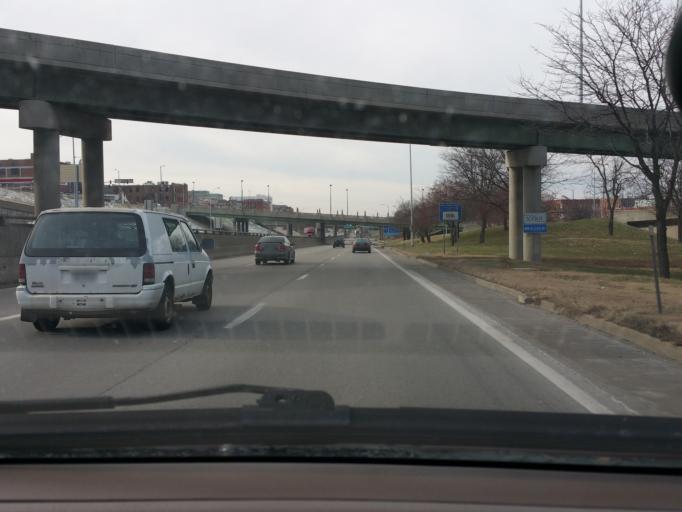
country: US
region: Missouri
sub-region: Jackson County
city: Kansas City
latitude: 39.1068
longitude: -94.5777
